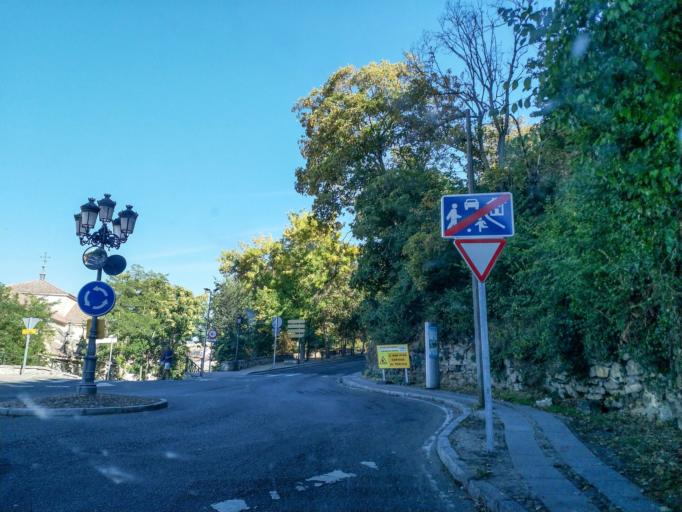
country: ES
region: Castille and Leon
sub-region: Provincia de Segovia
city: Segovia
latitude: 40.9524
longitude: -4.1200
